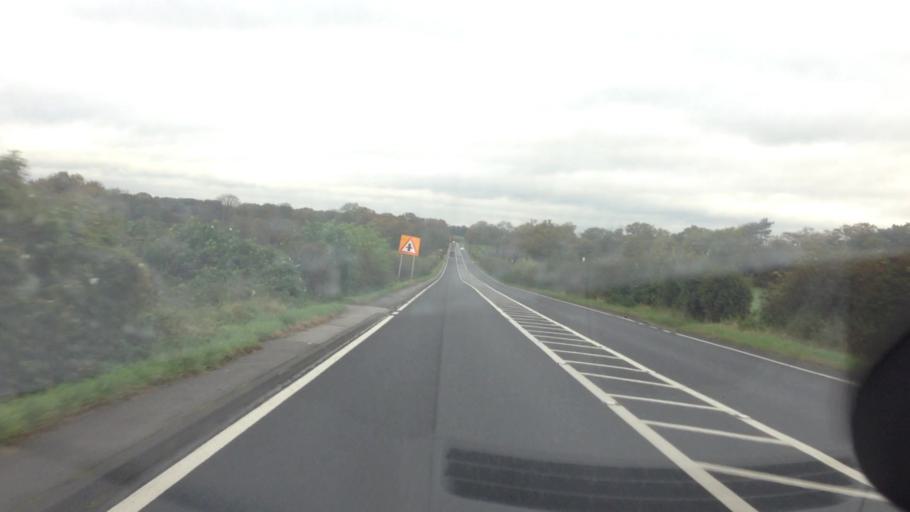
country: GB
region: England
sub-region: City and Borough of Leeds
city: Shadwell
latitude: 53.8466
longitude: -1.4659
